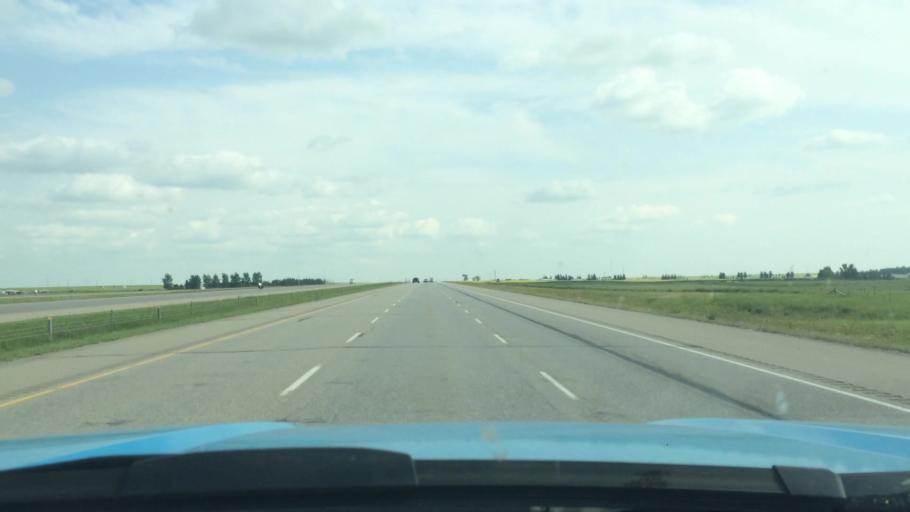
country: CA
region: Alberta
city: Crossfield
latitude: 51.4580
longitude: -114.0213
